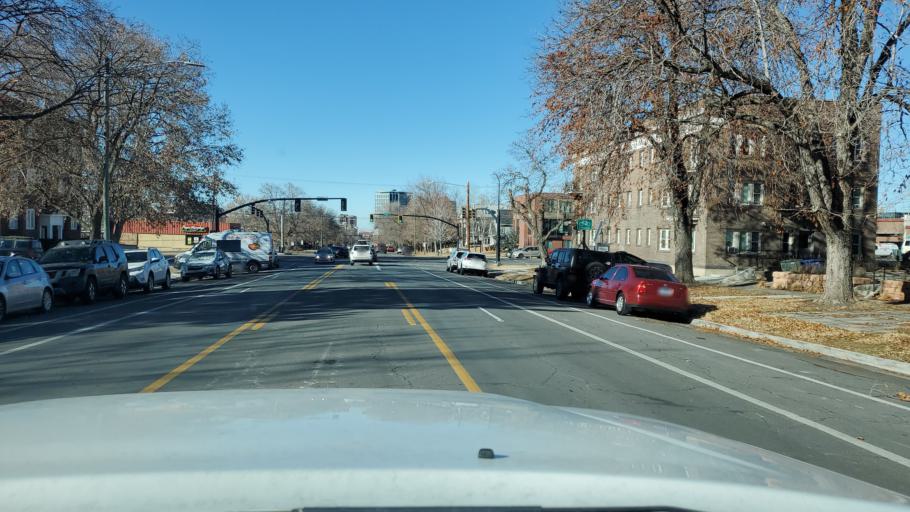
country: US
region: Utah
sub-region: Salt Lake County
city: Salt Lake City
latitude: 40.7629
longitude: -111.8700
